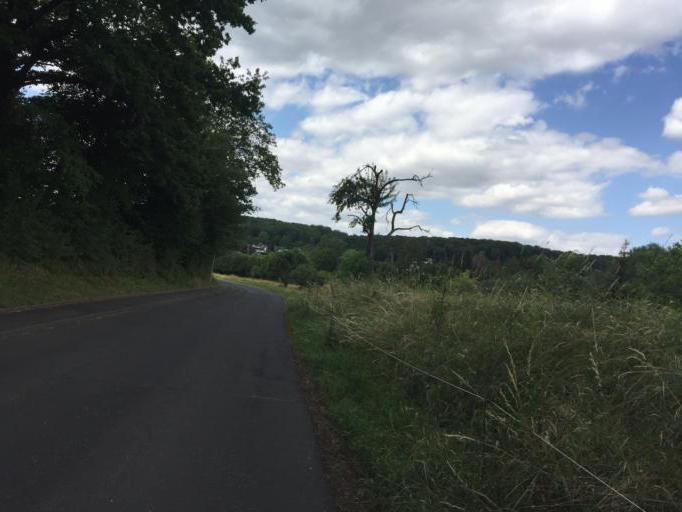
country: DE
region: Hesse
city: Lollar
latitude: 50.6440
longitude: 8.6768
